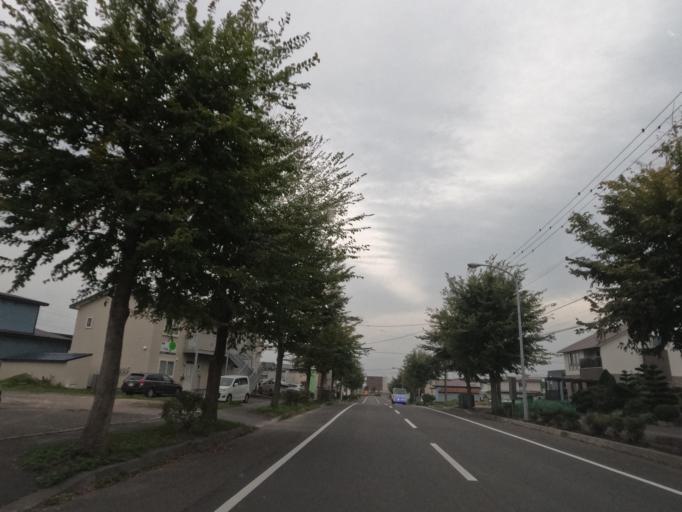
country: JP
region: Hokkaido
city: Date
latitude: 42.4637
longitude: 140.8731
